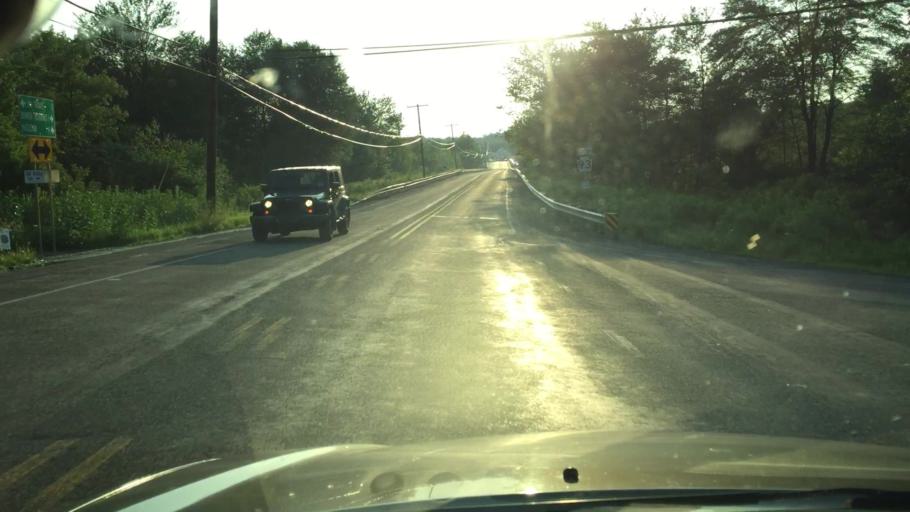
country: US
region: Pennsylvania
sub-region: Luzerne County
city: Oakdale
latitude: 40.9269
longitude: -75.9036
